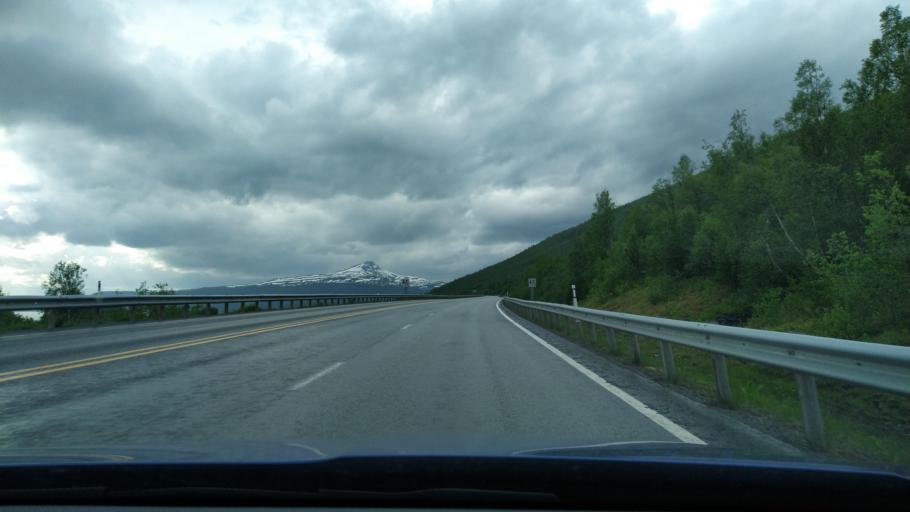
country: NO
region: Troms
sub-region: Balsfjord
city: Storsteinnes
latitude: 69.2300
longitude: 19.4891
